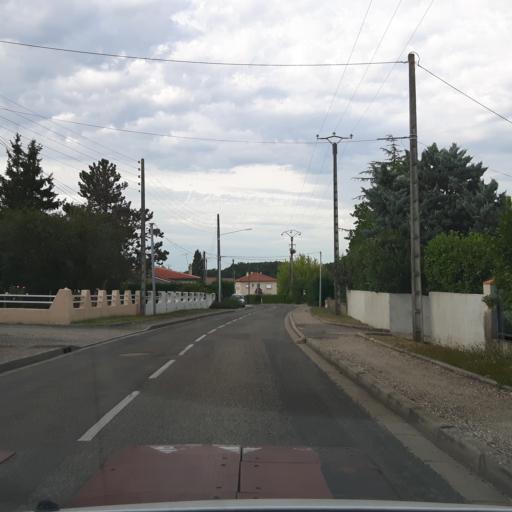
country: FR
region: Midi-Pyrenees
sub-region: Departement de la Haute-Garonne
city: Fronton
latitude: 43.8365
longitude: 1.3833
